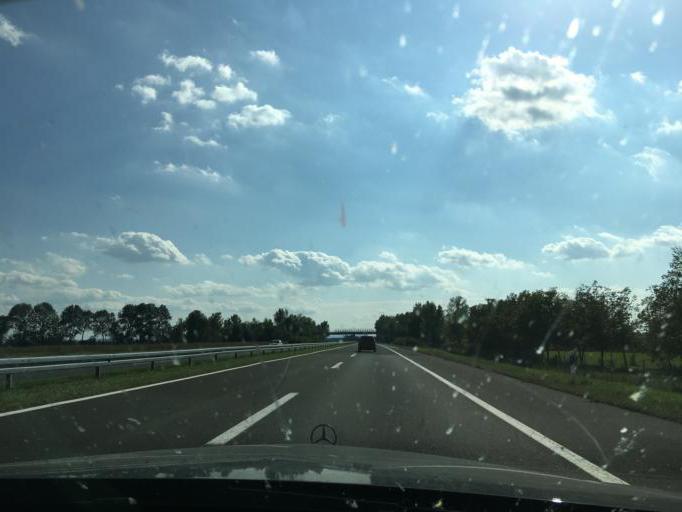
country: HR
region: Medimurska
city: Mala Subotica
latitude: 46.3605
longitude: 16.5390
